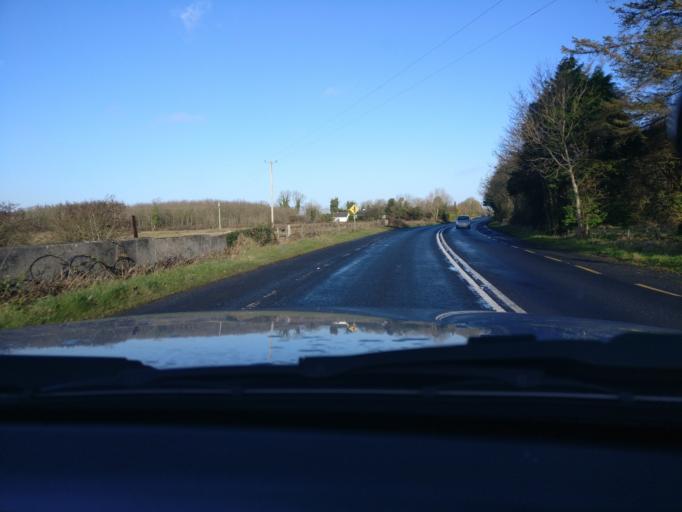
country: IE
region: Connaught
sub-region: County Galway
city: Loughrea
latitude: 53.2421
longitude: -8.4505
